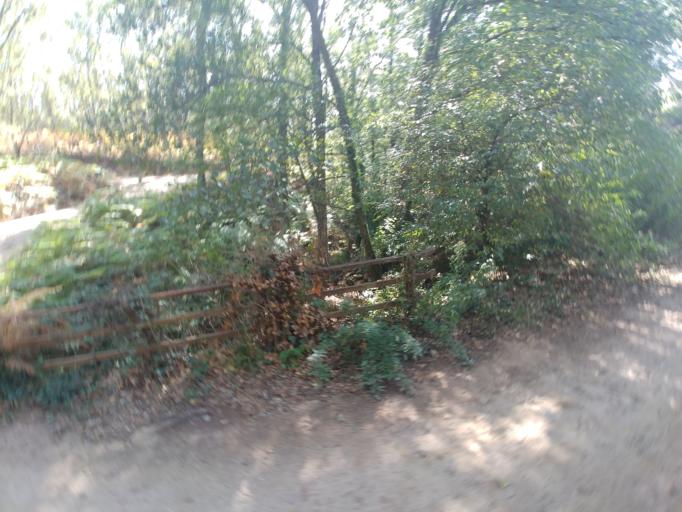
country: ES
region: Extremadura
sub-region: Provincia de Caceres
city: Garganta la Olla
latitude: 40.1001
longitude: -5.7418
